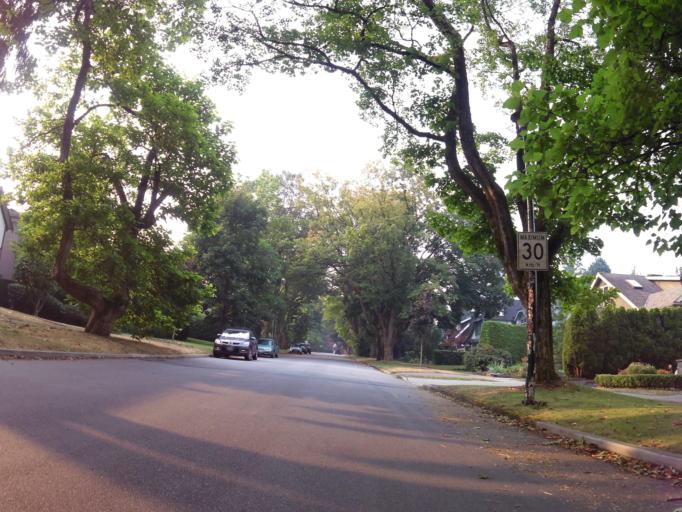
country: CA
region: British Columbia
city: Vancouver
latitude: 49.2410
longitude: -123.1456
